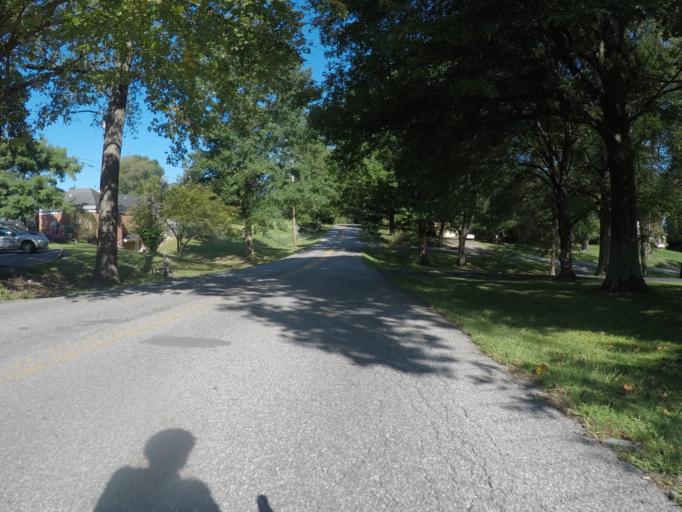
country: US
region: Kentucky
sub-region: Boyd County
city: Westwood
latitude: 38.4914
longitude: -82.6930
